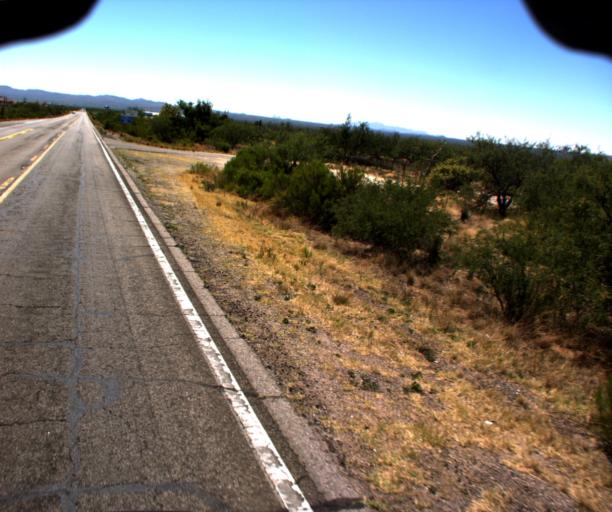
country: US
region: Arizona
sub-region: Pinal County
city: Oracle
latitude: 32.6196
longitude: -110.8077
